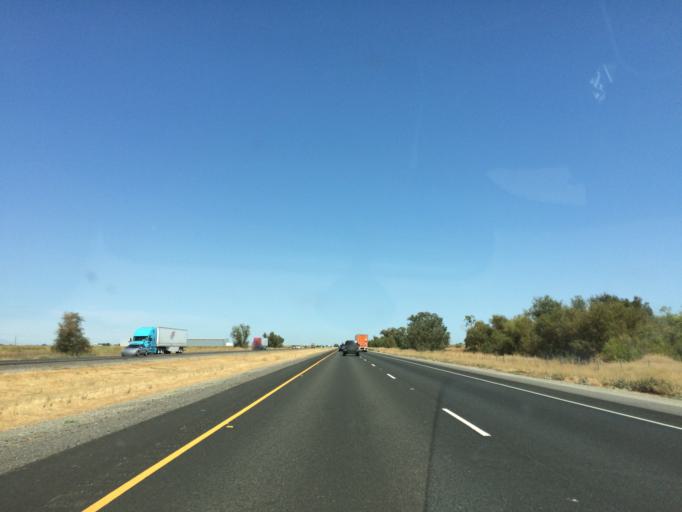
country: US
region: California
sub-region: Colusa County
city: Maxwell
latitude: 39.3803
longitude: -122.1928
